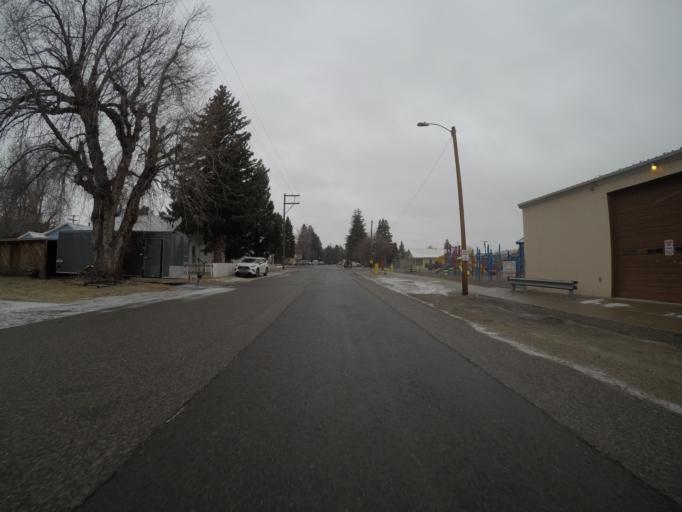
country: US
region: Montana
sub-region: Stillwater County
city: Absarokee
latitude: 45.5164
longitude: -109.4447
